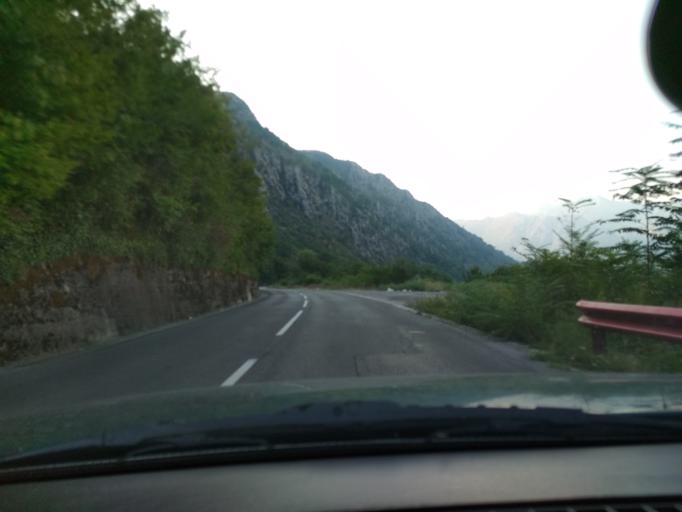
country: ME
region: Kotor
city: Kotor
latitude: 42.4118
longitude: 18.7638
